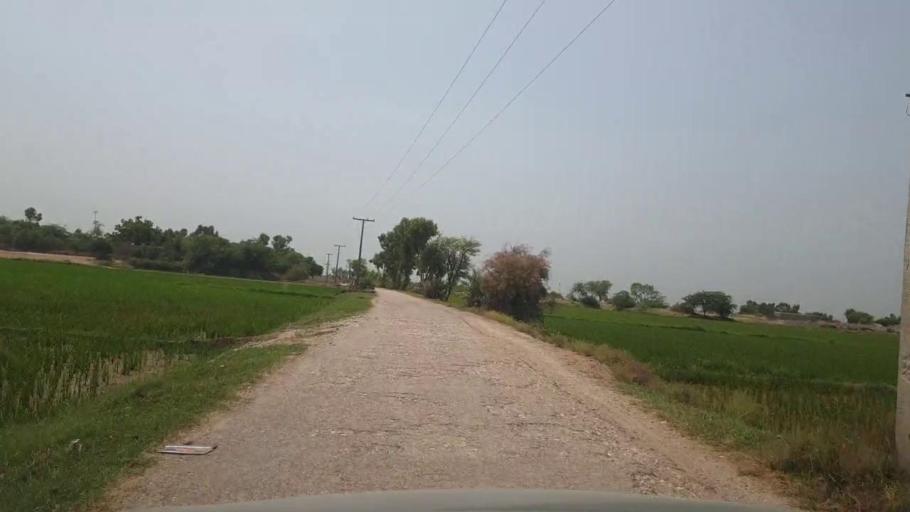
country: PK
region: Sindh
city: Garhi Yasin
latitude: 27.9300
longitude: 68.4009
